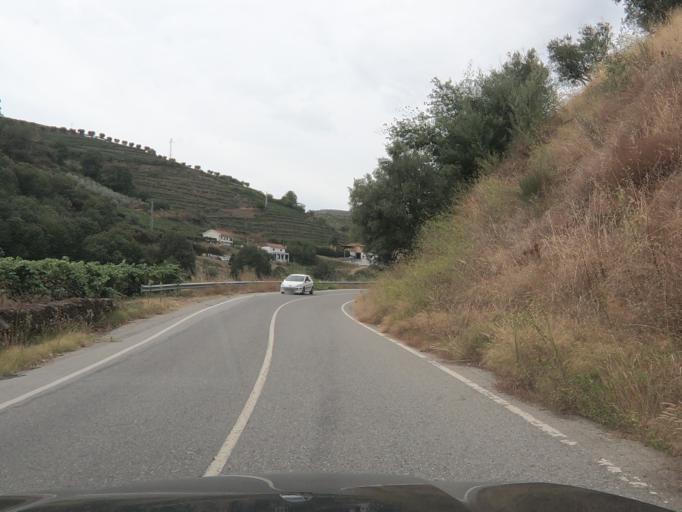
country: PT
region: Vila Real
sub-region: Santa Marta de Penaguiao
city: Santa Marta de Penaguiao
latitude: 41.2186
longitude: -7.7769
